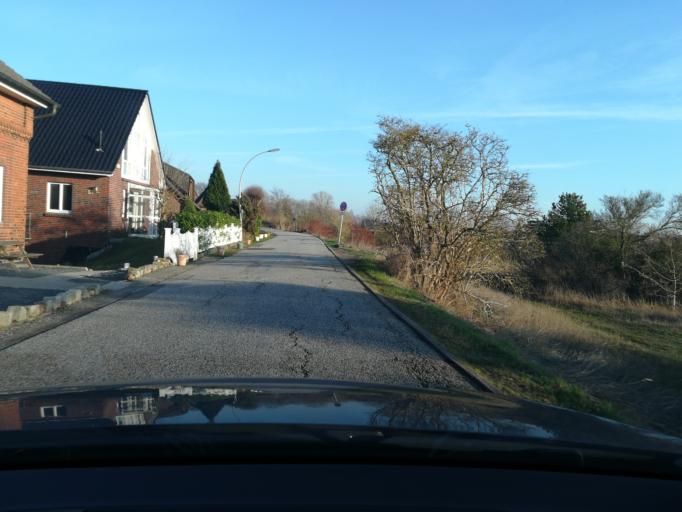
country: DE
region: Lower Saxony
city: Stelle
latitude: 53.4492
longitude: 10.0917
